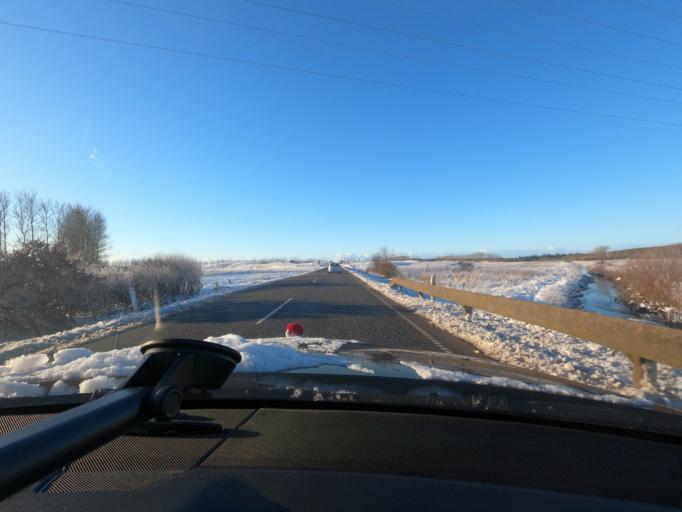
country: DK
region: South Denmark
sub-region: Tonder Kommune
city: Sherrebek
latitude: 55.1762
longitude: 8.8311
